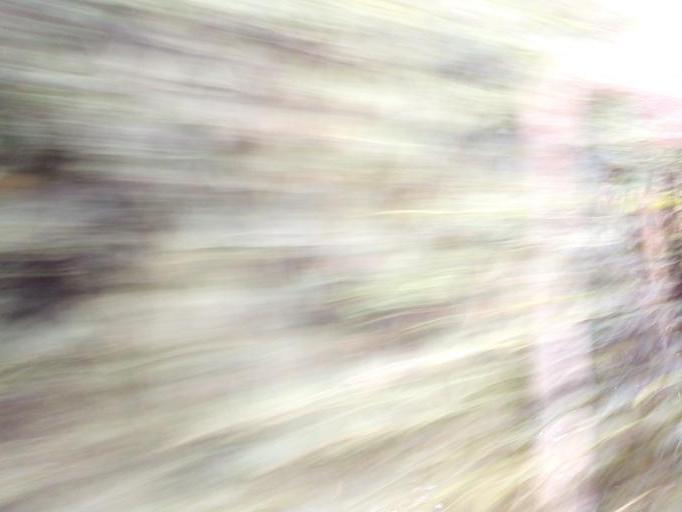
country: BD
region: Dhaka
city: Nagarpur
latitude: 23.8497
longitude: 89.8941
